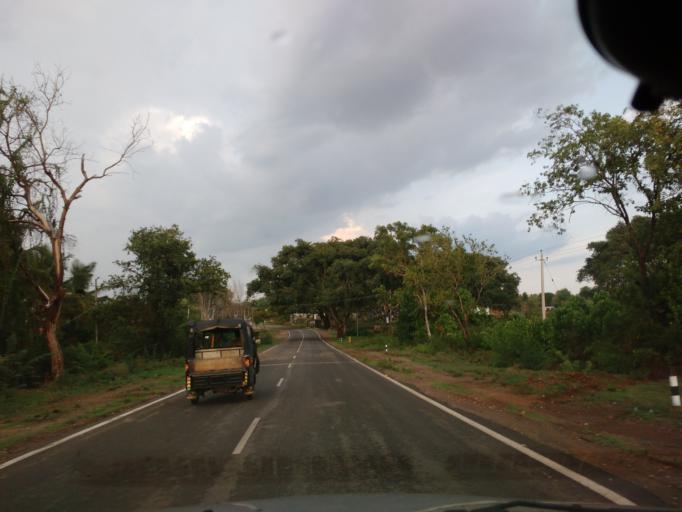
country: IN
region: Karnataka
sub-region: Tumkur
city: Tiptur
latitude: 13.2678
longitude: 76.4169
